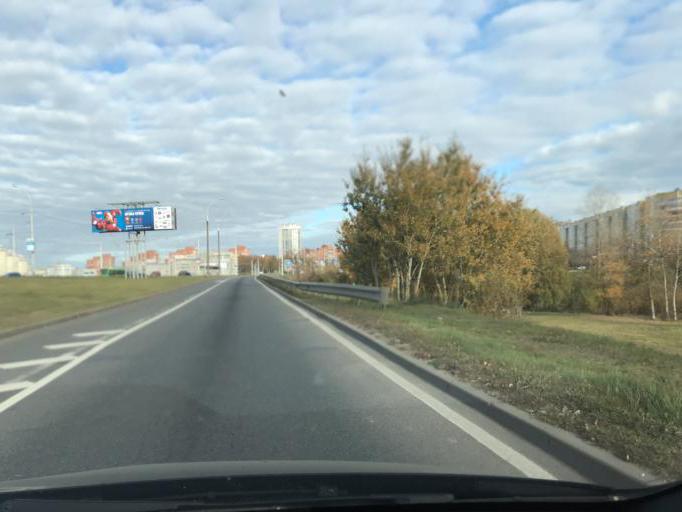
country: BY
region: Minsk
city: Borovlyany
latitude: 53.9411
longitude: 27.6766
